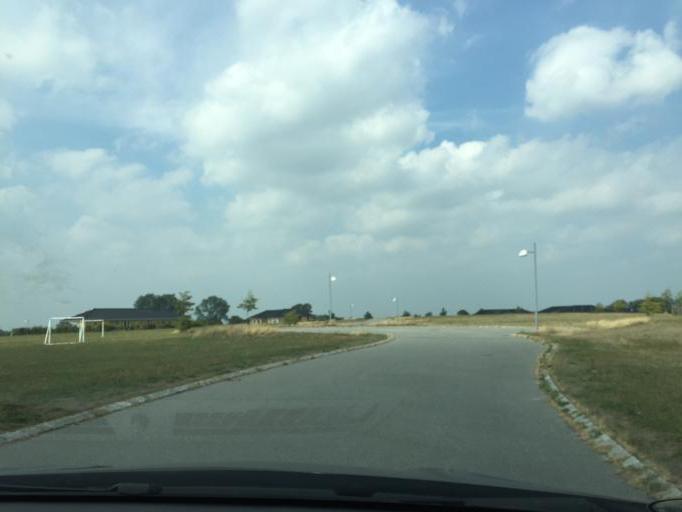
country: DK
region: South Denmark
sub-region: Nyborg Kommune
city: Nyborg
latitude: 55.3160
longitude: 10.7612
